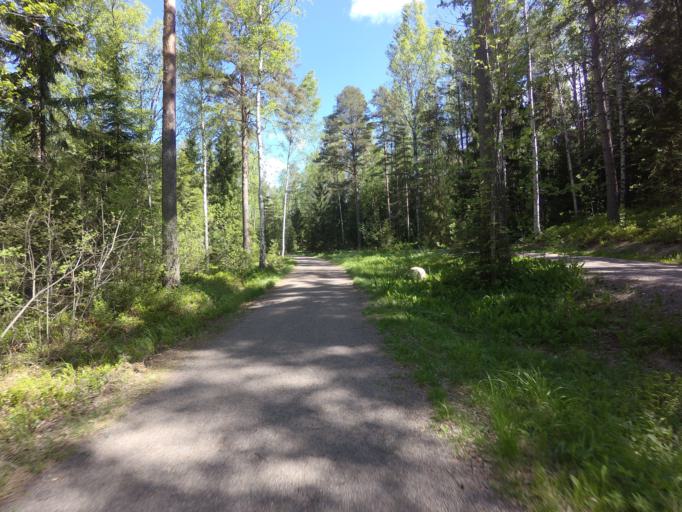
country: FI
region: Uusimaa
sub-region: Helsinki
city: Kauniainen
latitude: 60.1823
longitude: 24.7246
